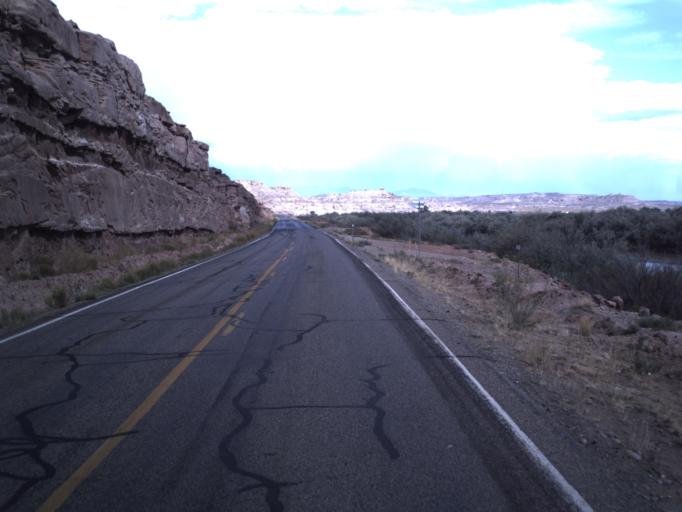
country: US
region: Utah
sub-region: San Juan County
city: Blanding
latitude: 37.2574
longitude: -109.2879
